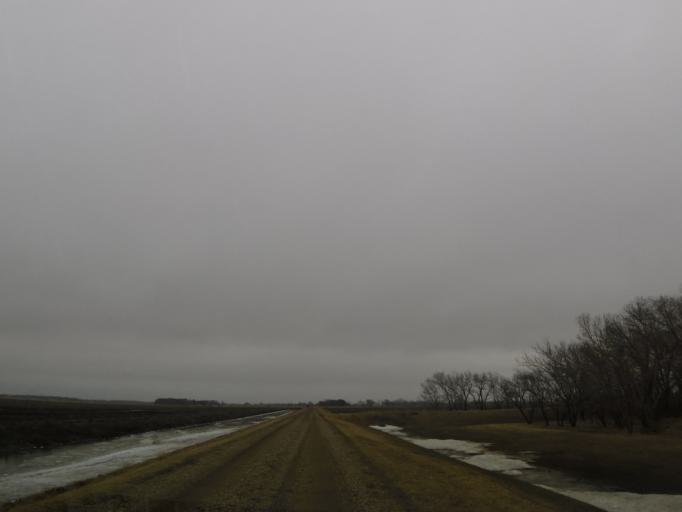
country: US
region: North Dakota
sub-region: Walsh County
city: Grafton
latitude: 48.3686
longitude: -97.1743
